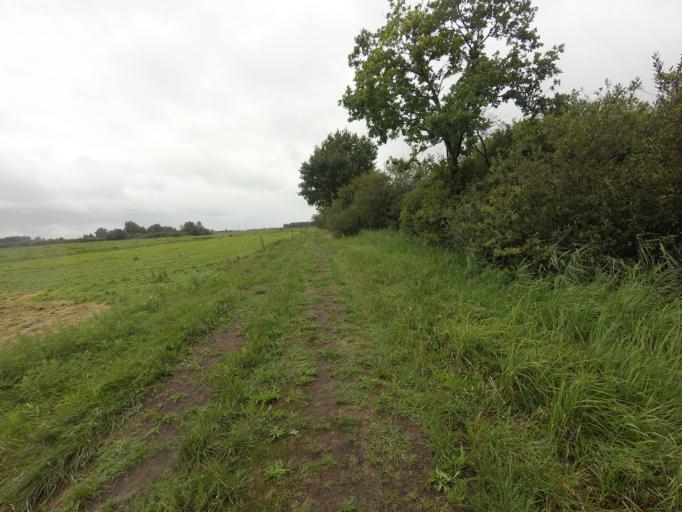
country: NL
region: Overijssel
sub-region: Gemeente Steenwijkerland
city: Blokzijl
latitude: 52.7653
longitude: 5.9798
